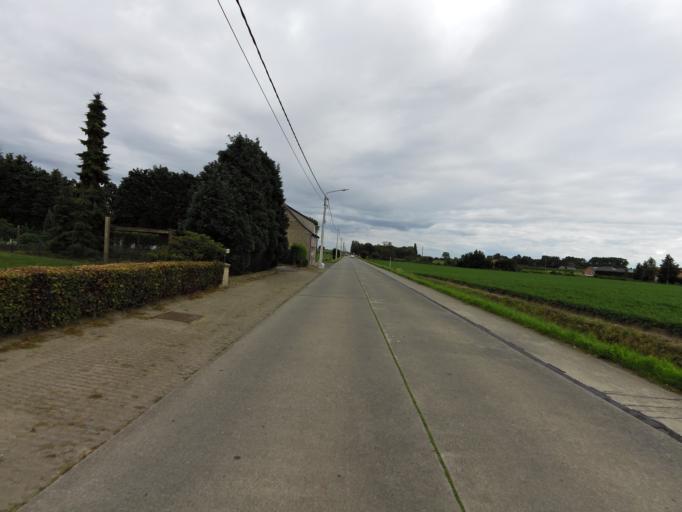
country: BE
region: Flanders
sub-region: Provincie West-Vlaanderen
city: Ichtegem
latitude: 51.0599
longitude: 3.0065
